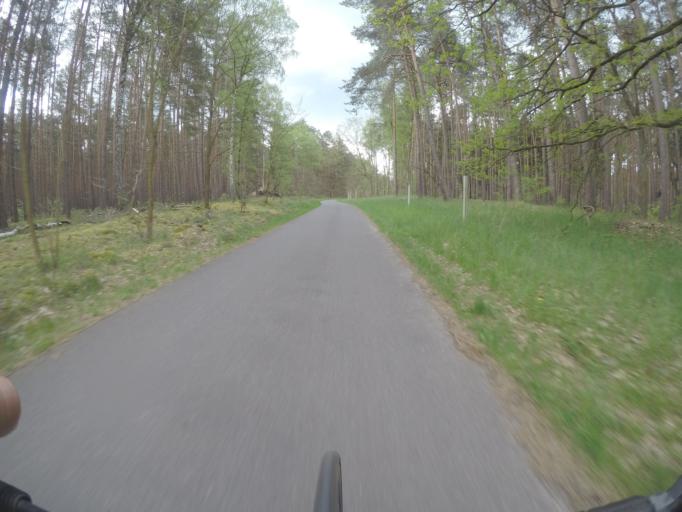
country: DE
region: Brandenburg
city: Biesenthal
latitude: 52.7885
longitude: 13.6353
